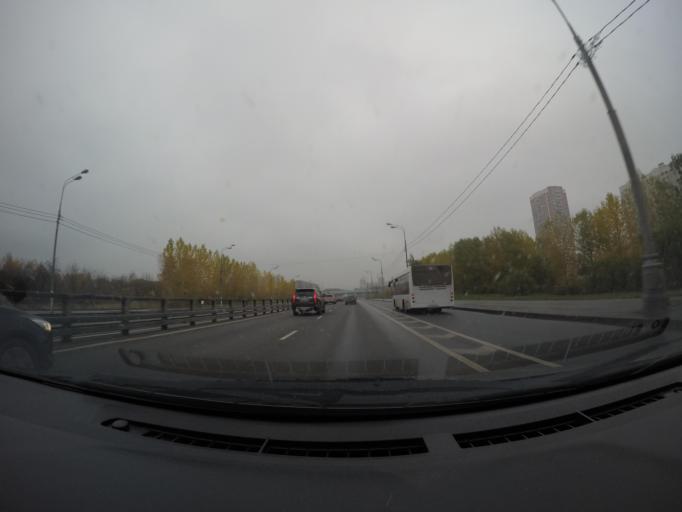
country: RU
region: Moskovskaya
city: Shcherbinka
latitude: 55.5292
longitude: 37.5806
